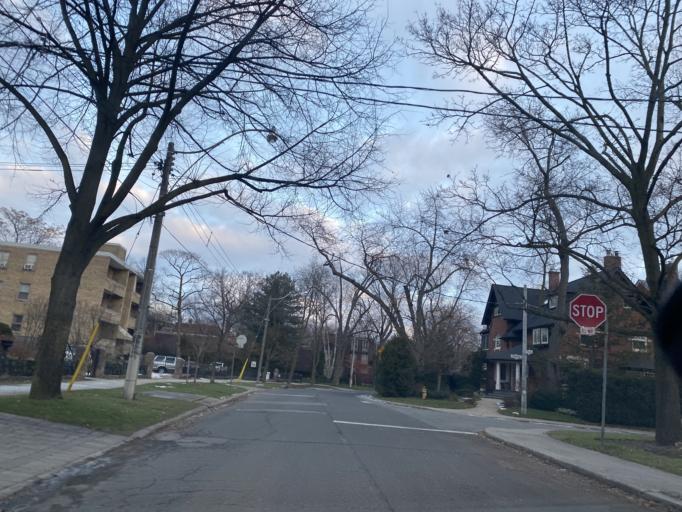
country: CA
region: Ontario
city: Toronto
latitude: 43.6752
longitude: -79.3739
